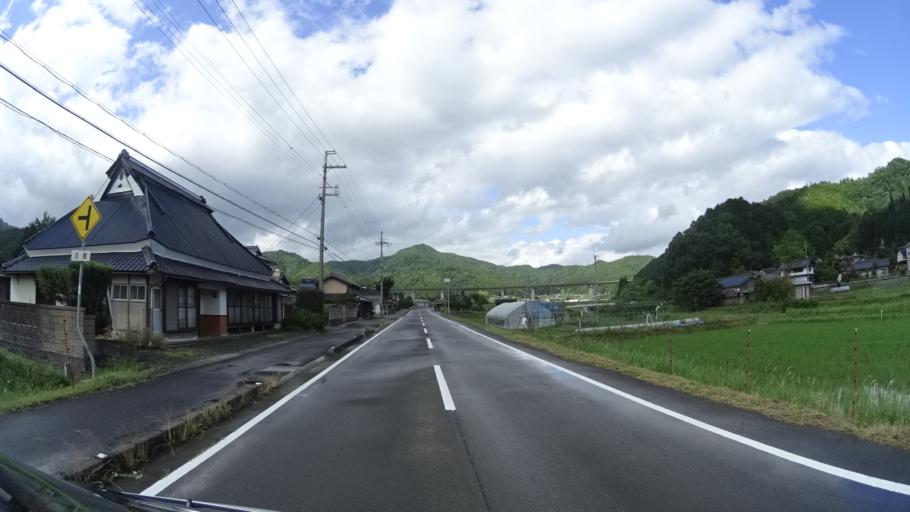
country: JP
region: Kyoto
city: Ayabe
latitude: 35.3813
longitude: 135.2391
